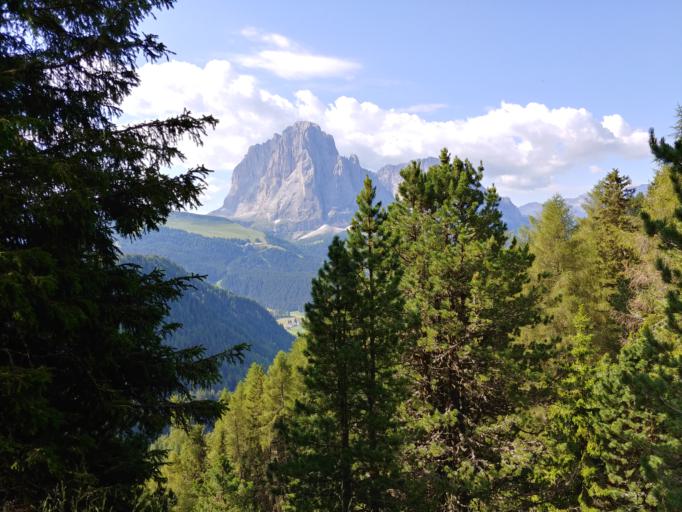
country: IT
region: Trentino-Alto Adige
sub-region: Bolzano
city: Santa Cristina Valgardena
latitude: 46.5792
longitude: 11.7387
